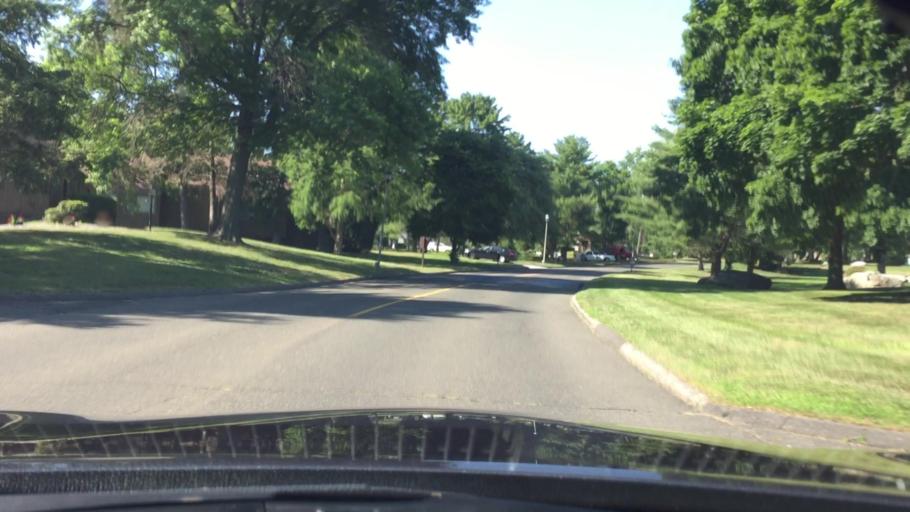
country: US
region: Connecticut
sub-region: New Haven County
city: City of Milford (balance)
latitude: 41.2491
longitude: -73.1108
